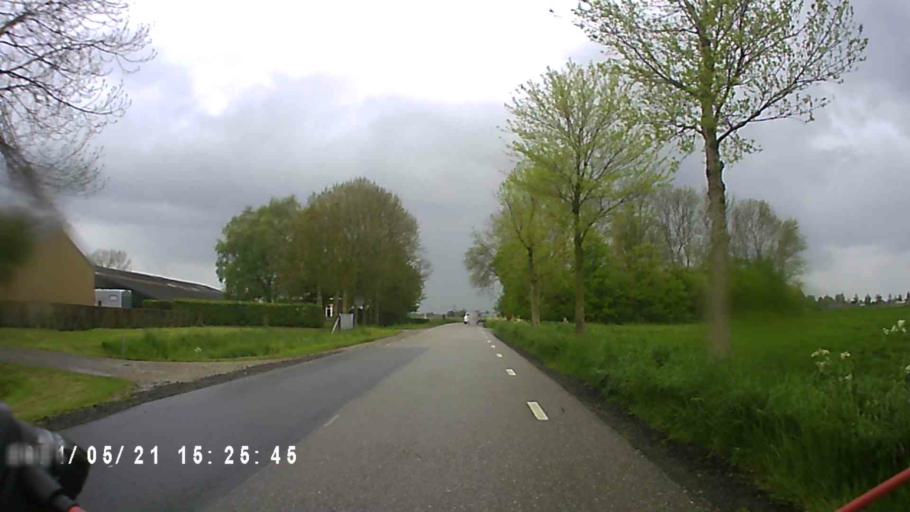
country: NL
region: Groningen
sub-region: Gemeente Zuidhorn
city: Aduard
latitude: 53.2318
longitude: 6.4583
